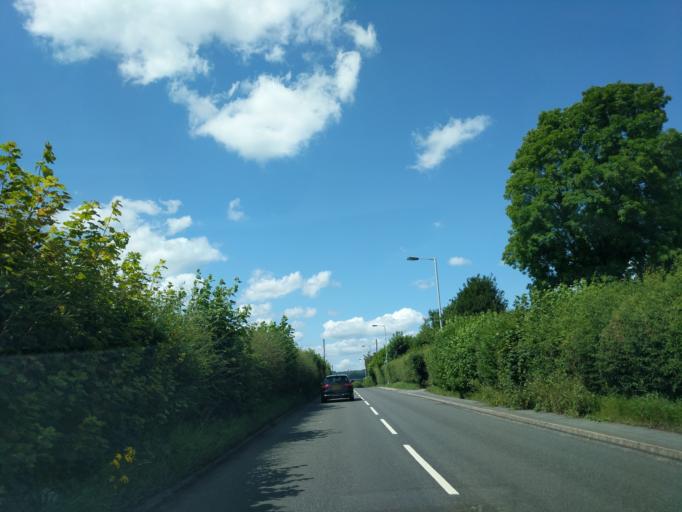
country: GB
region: England
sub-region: Staffordshire
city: Cheadle
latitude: 52.9464
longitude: -1.9795
